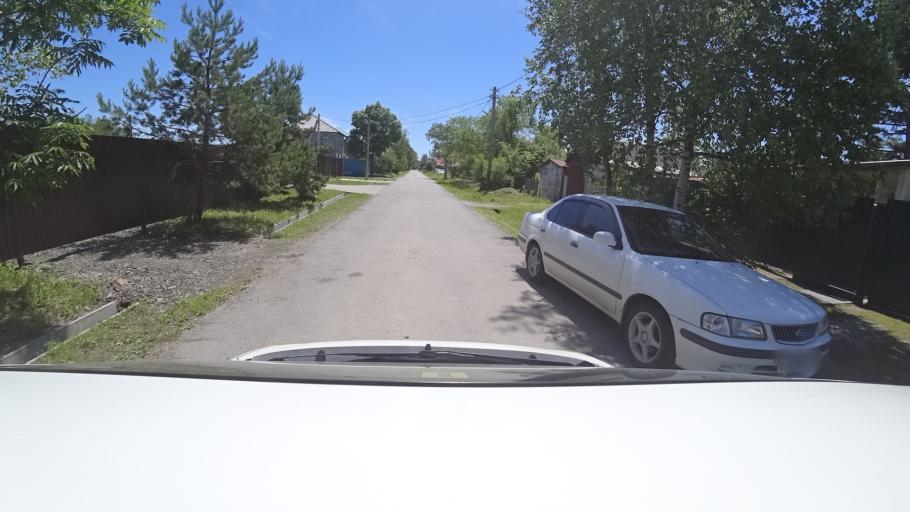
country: RU
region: Khabarovsk Krai
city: Topolevo
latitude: 48.5118
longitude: 135.1743
